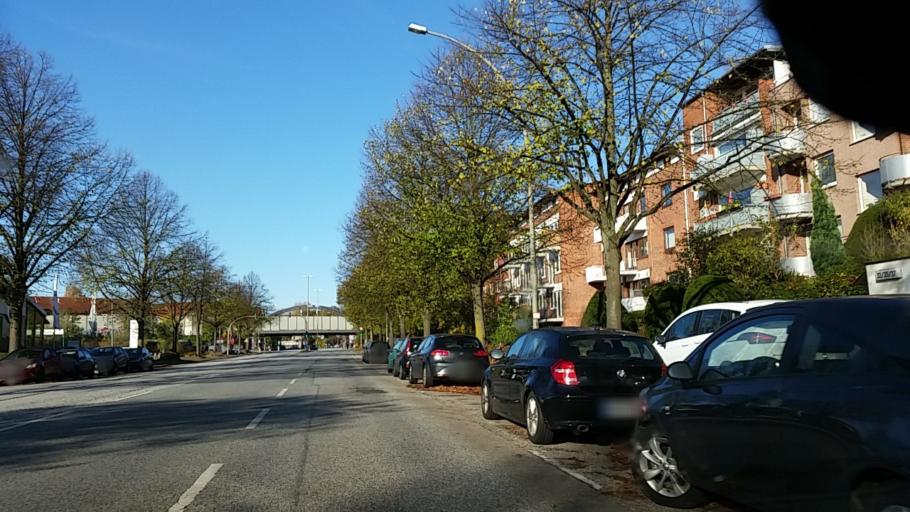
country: DE
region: Hamburg
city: Marienthal
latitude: 53.5527
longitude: 10.0707
